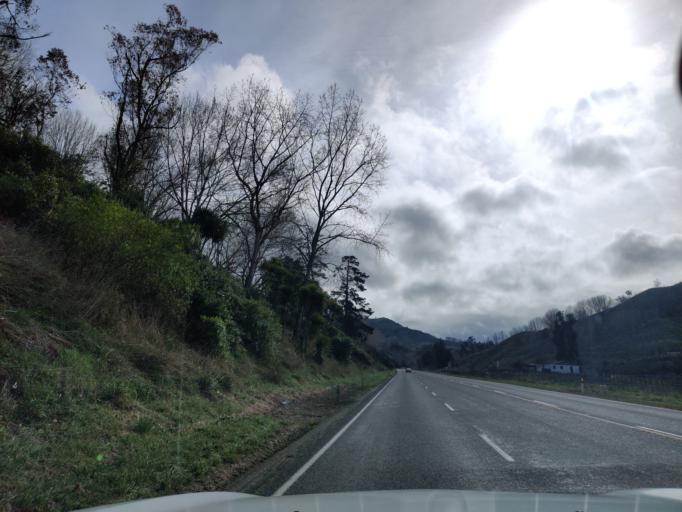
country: NZ
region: Manawatu-Wanganui
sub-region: Ruapehu District
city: Waiouru
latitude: -39.7888
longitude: 175.7852
